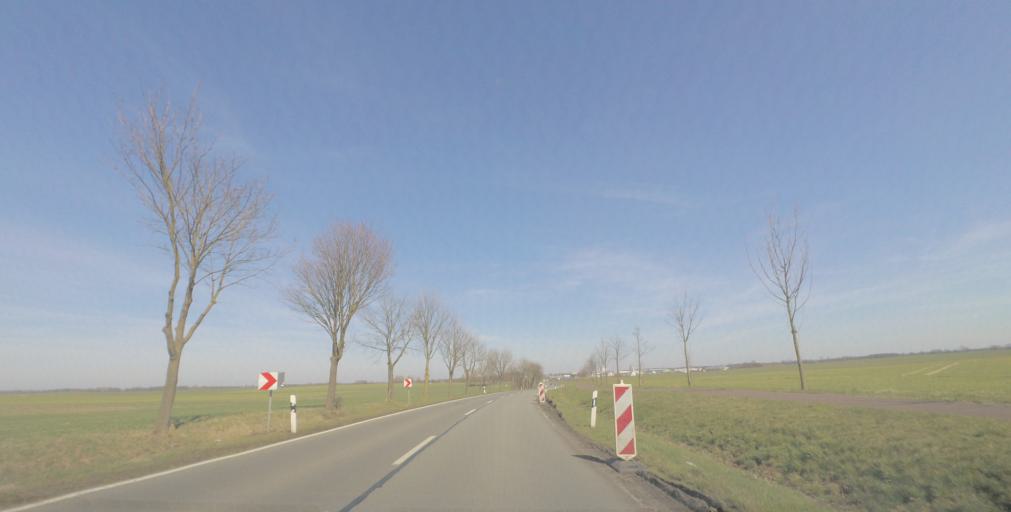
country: DE
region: Brandenburg
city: Fehrbellin
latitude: 52.8710
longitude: 12.7818
